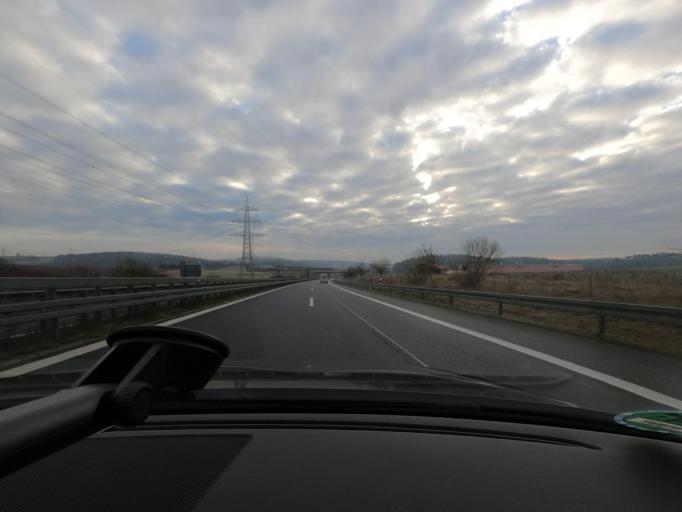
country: DE
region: Bavaria
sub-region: Upper Franconia
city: Rodental
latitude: 50.2467
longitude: 11.0394
